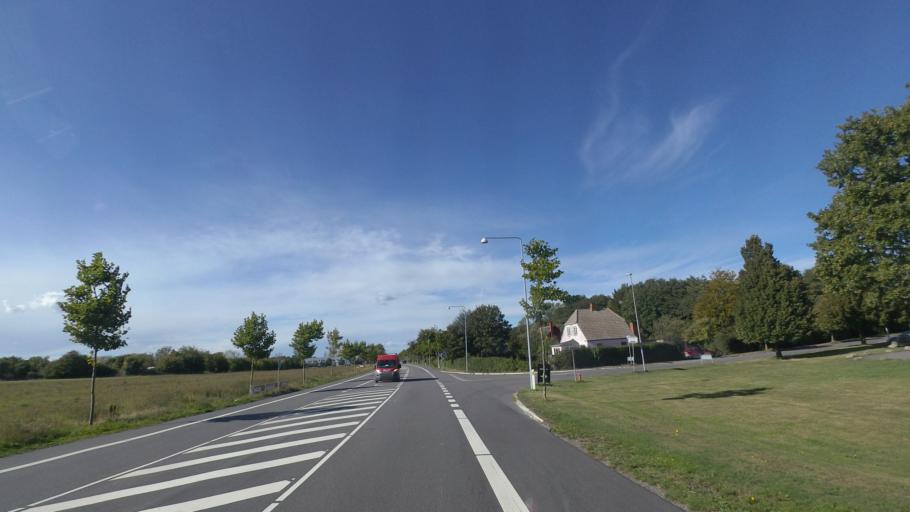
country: DK
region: Capital Region
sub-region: Bornholm Kommune
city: Ronne
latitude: 55.0908
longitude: 14.7357
